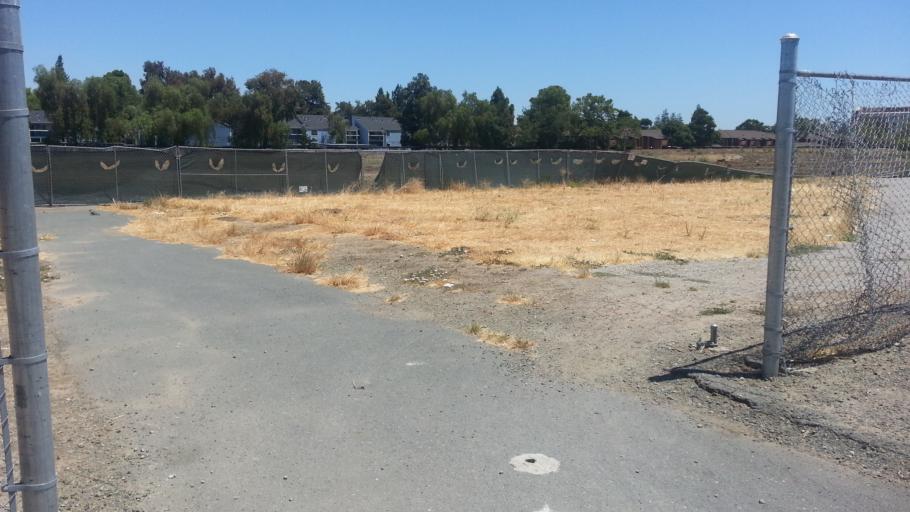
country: US
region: California
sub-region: Contra Costa County
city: Pittsburg
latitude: 38.0062
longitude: -121.8758
